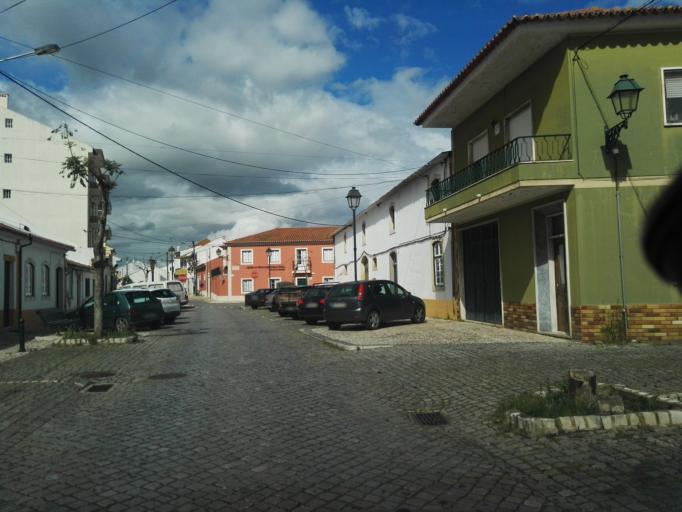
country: PT
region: Santarem
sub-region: Golega
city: Golega
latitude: 39.4042
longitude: -8.4837
